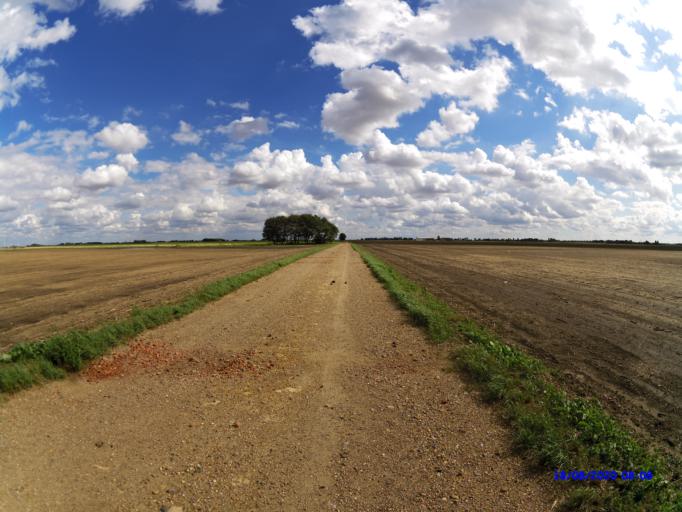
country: GB
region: England
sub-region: Cambridgeshire
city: Whittlesey
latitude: 52.5123
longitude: -0.0833
